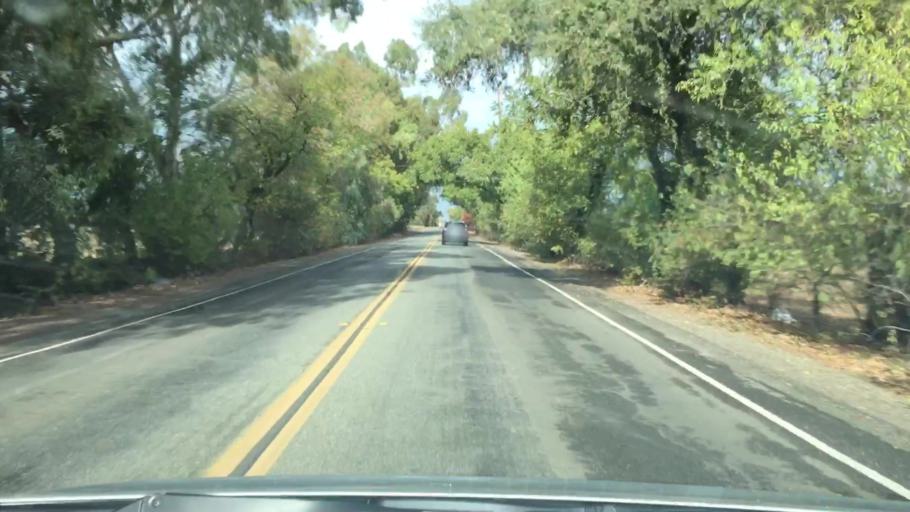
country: US
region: California
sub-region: Yolo County
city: Davis
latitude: 38.5527
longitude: -121.8033
